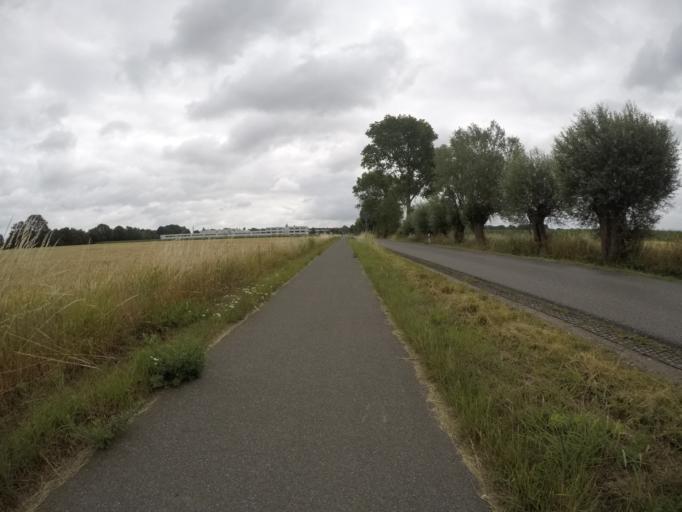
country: DE
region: North Rhine-Westphalia
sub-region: Regierungsbezirk Dusseldorf
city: Bocholt
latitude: 51.8083
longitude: 6.5971
